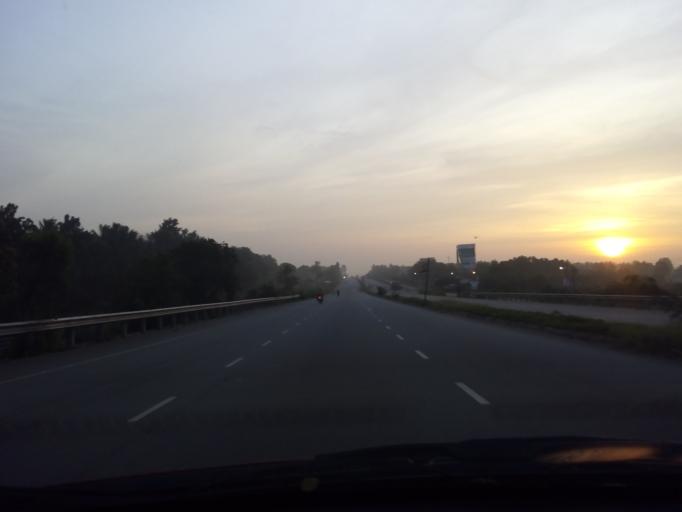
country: IN
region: Karnataka
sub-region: Bangalore Rural
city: Devanhalli
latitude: 13.2200
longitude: 77.6809
